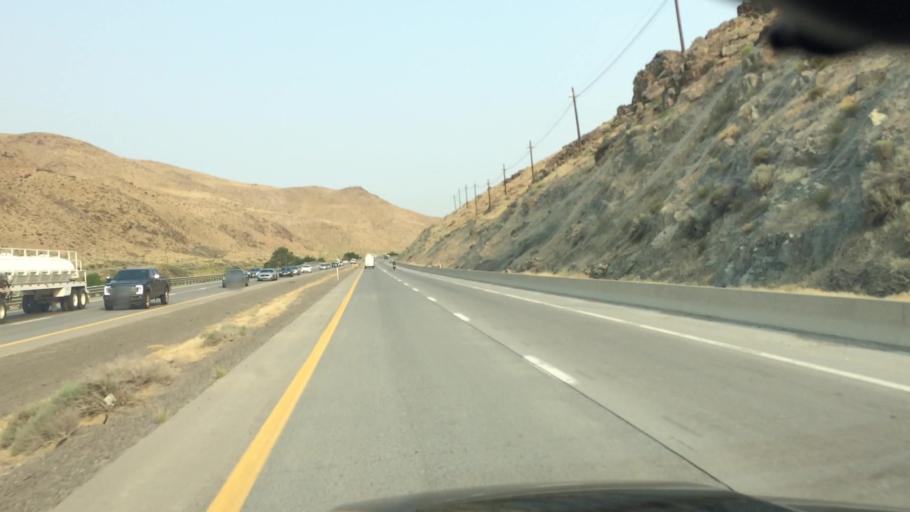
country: US
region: Nevada
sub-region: Washoe County
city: Sparks
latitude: 39.5122
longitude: -119.6706
